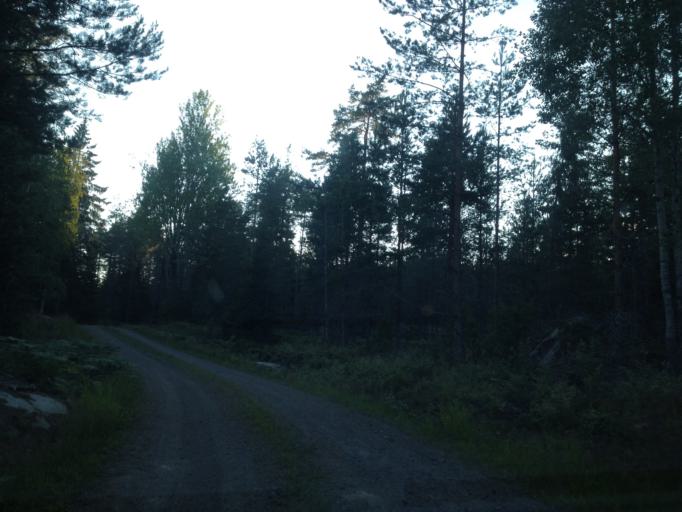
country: SE
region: Kalmar
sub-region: Vasterviks Kommun
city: Overum
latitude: 57.9982
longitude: 16.1664
